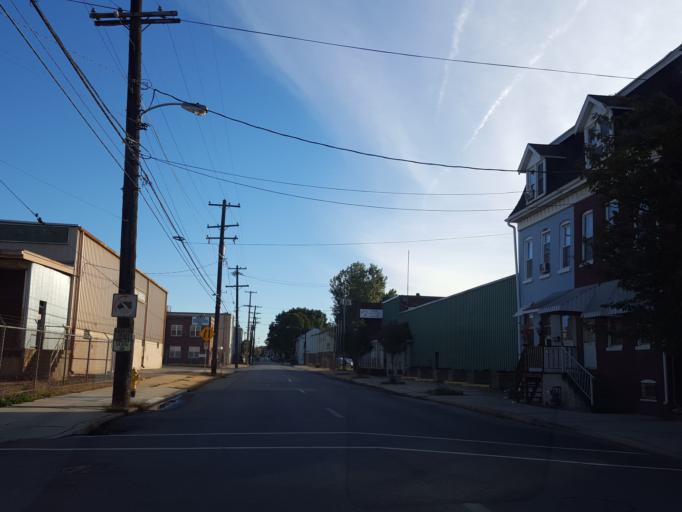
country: US
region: Pennsylvania
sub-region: York County
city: York
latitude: 39.9650
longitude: -76.7153
